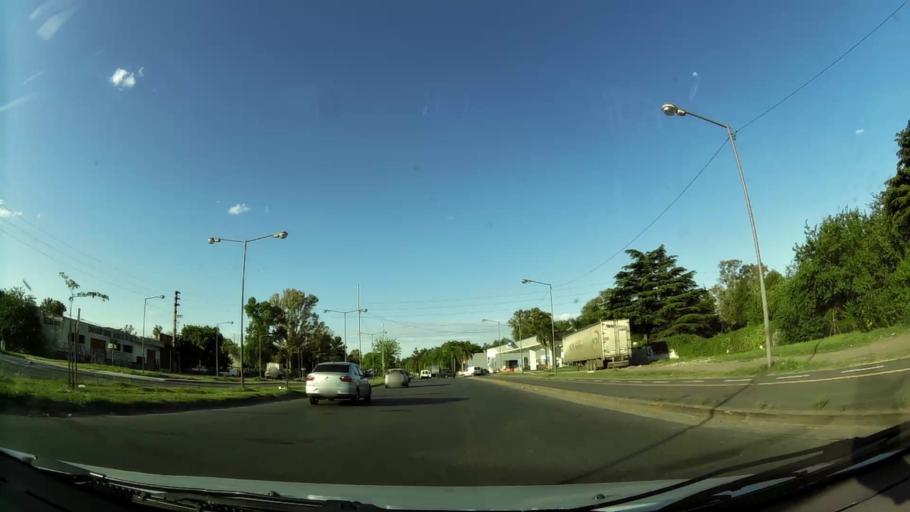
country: AR
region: Buenos Aires
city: Caseros
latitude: -34.5518
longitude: -58.5840
